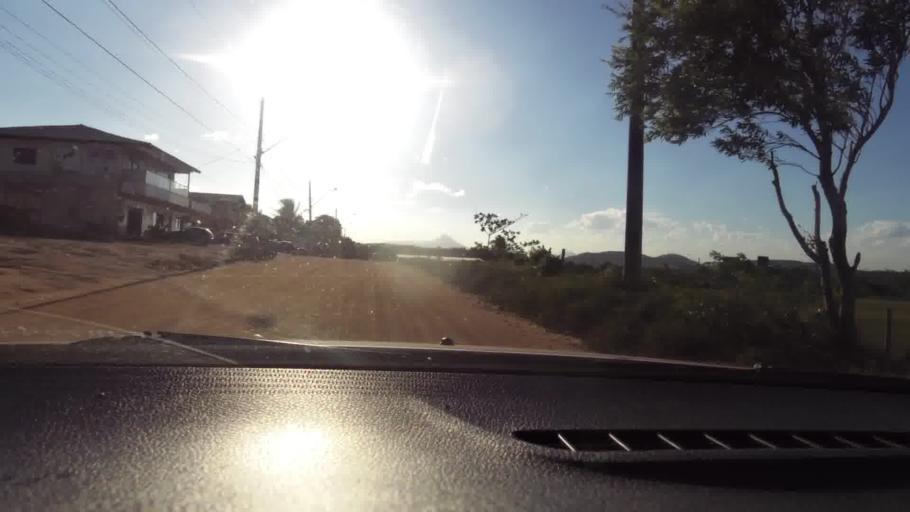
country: BR
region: Espirito Santo
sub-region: Guarapari
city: Guarapari
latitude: -20.5540
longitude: -40.4115
